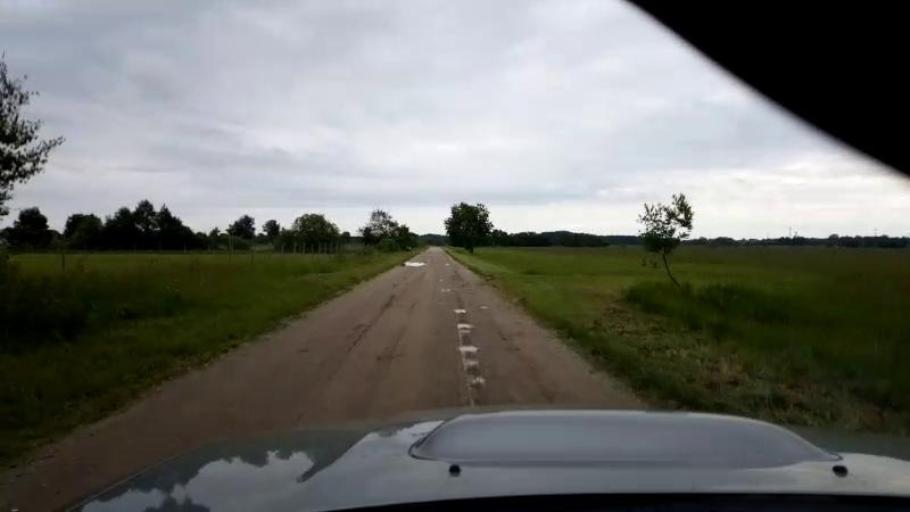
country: EE
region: Paernumaa
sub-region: Halinga vald
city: Parnu-Jaagupi
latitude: 58.5428
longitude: 24.5767
